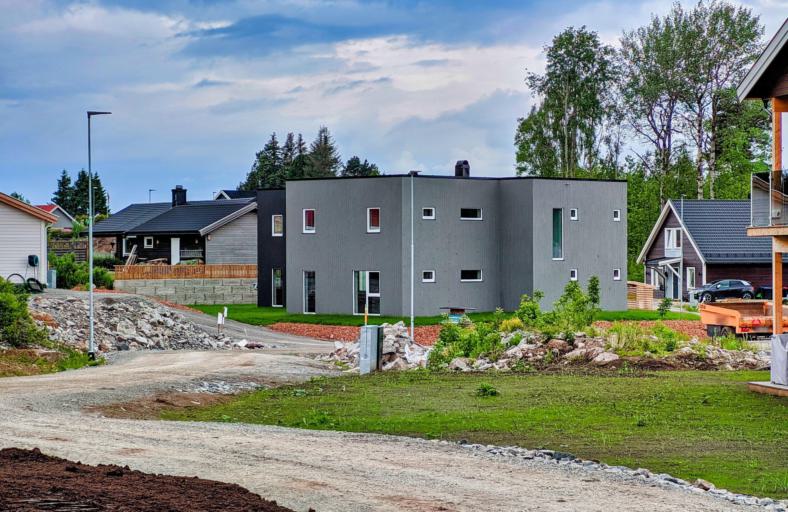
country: NO
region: Hedmark
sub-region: Stange
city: Stange
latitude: 60.7113
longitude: 11.2122
